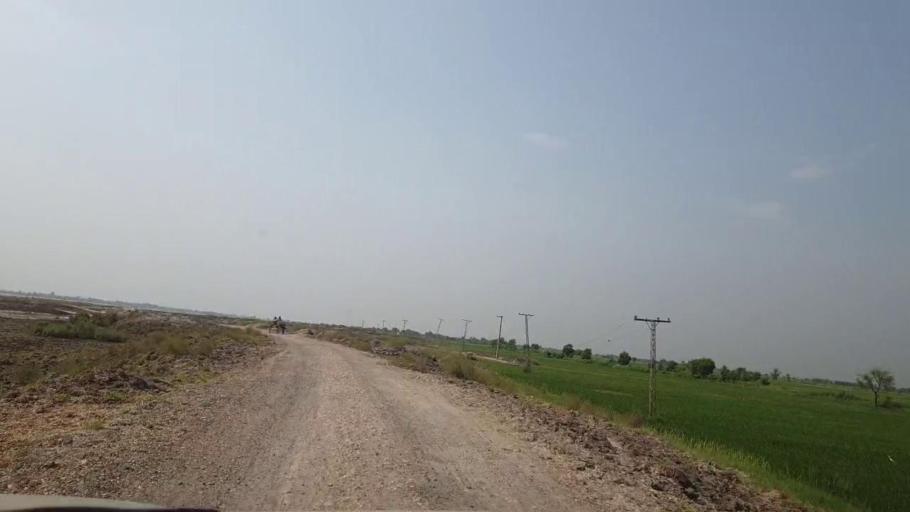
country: PK
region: Sindh
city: Dokri
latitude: 27.4251
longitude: 68.2040
